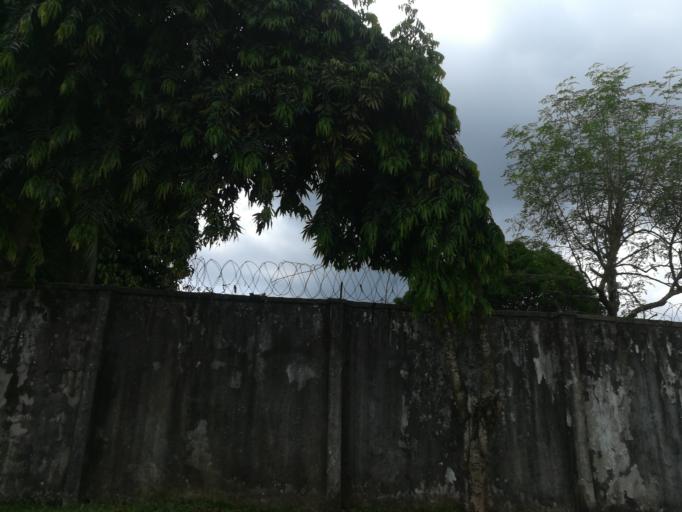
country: NG
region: Rivers
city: Okrika
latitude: 4.7311
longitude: 7.1453
